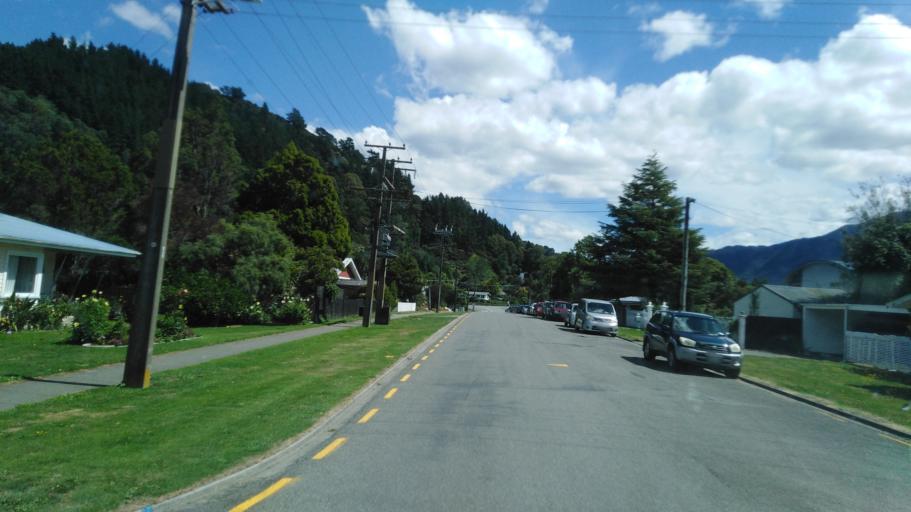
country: NZ
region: Marlborough
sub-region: Marlborough District
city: Picton
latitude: -41.2755
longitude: 173.7676
